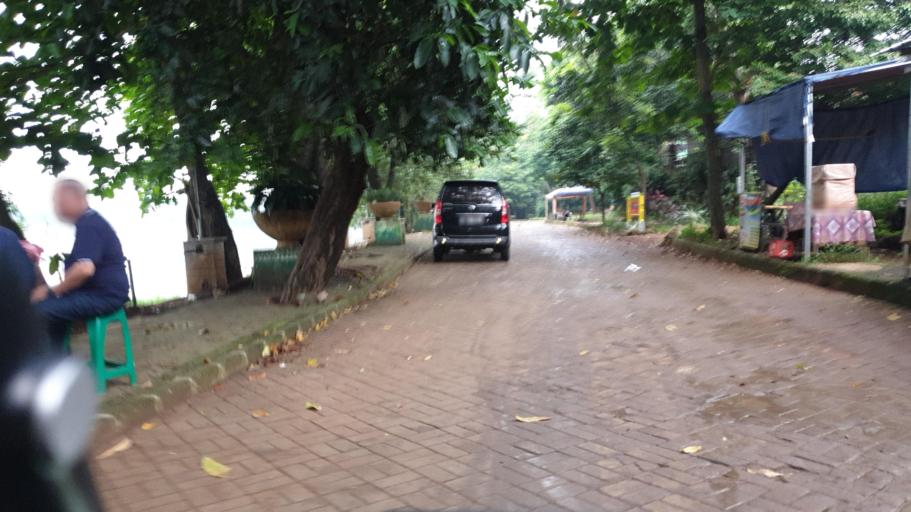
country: ID
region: West Java
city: Depok
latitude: -6.3407
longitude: 106.8232
